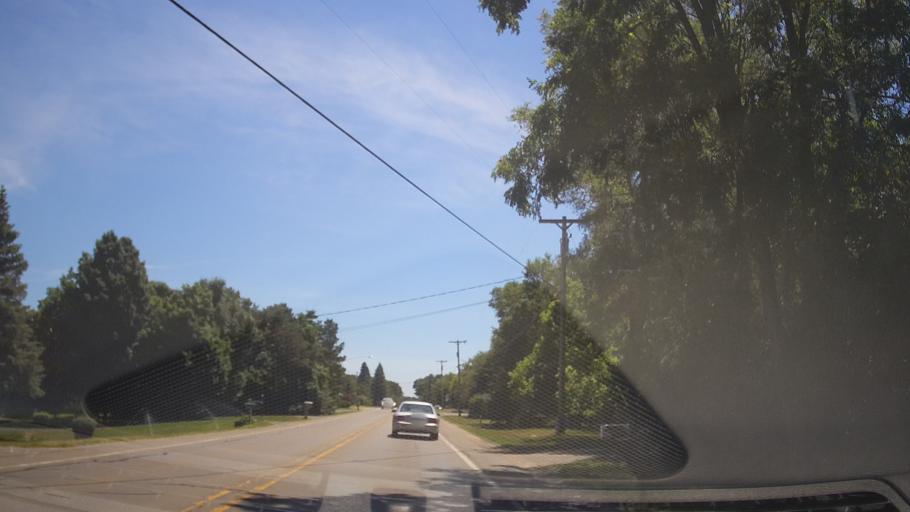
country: US
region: Michigan
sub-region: Grand Traverse County
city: Traverse City
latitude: 44.6954
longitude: -85.6916
